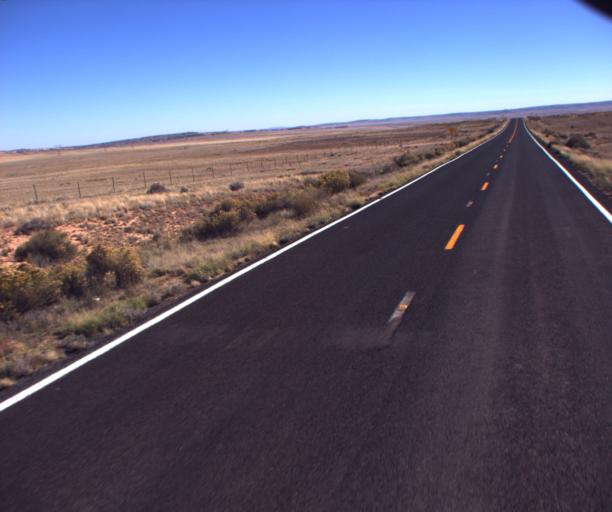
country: US
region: Arizona
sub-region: Coconino County
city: Tuba City
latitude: 35.9708
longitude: -110.8275
